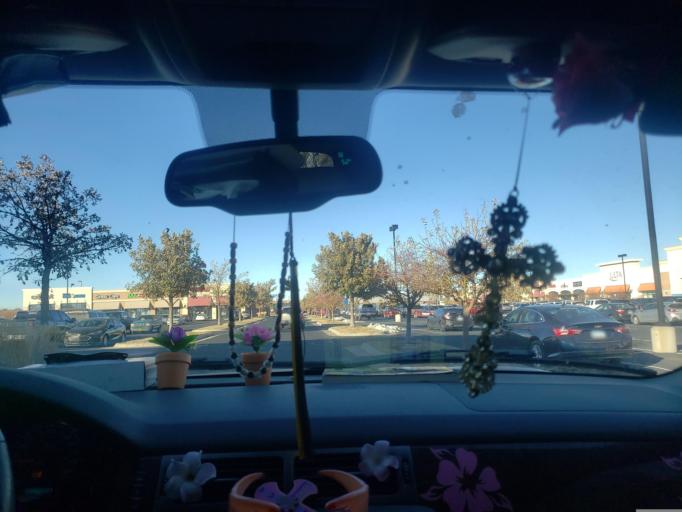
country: US
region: Kansas
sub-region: Finney County
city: Garden City
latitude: 37.9783
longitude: -100.8358
